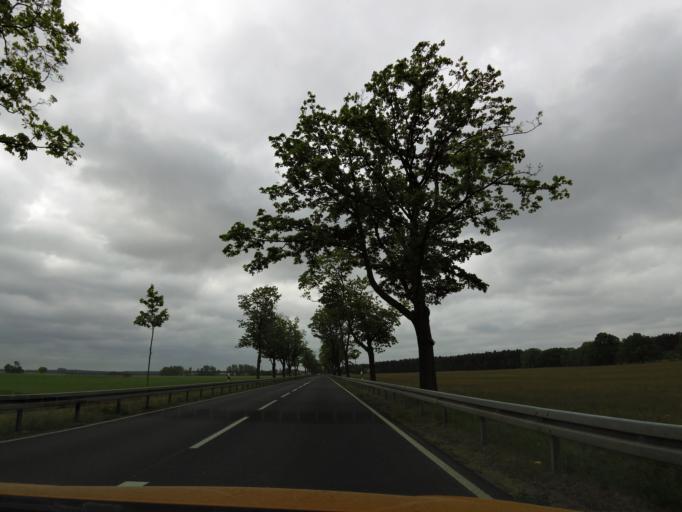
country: DE
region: Brandenburg
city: Beelitz
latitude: 52.1704
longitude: 12.9282
